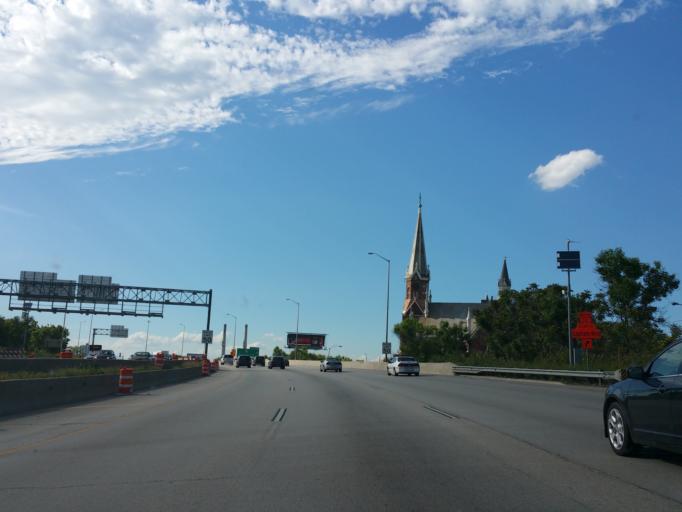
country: US
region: Wisconsin
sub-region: Milwaukee County
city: Milwaukee
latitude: 43.0179
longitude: -87.9162
